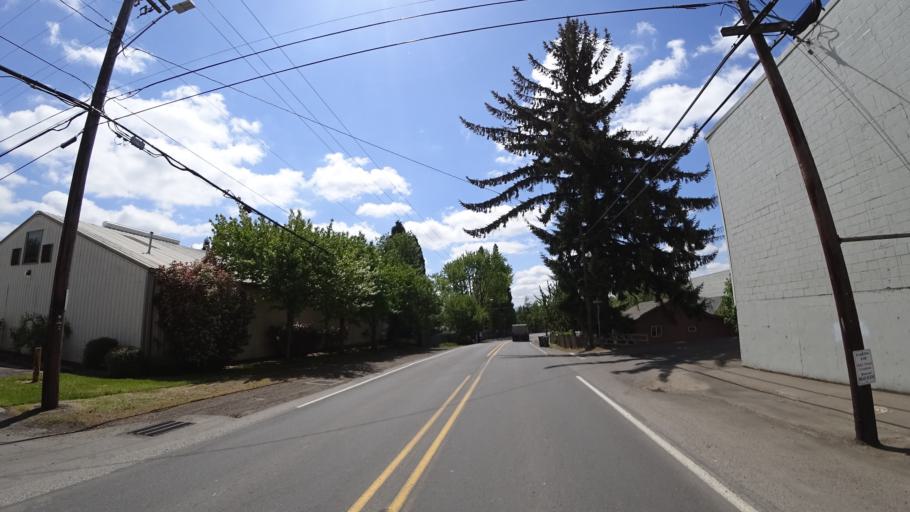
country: US
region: Oregon
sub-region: Washington County
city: Hillsboro
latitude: 45.5150
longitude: -122.9900
